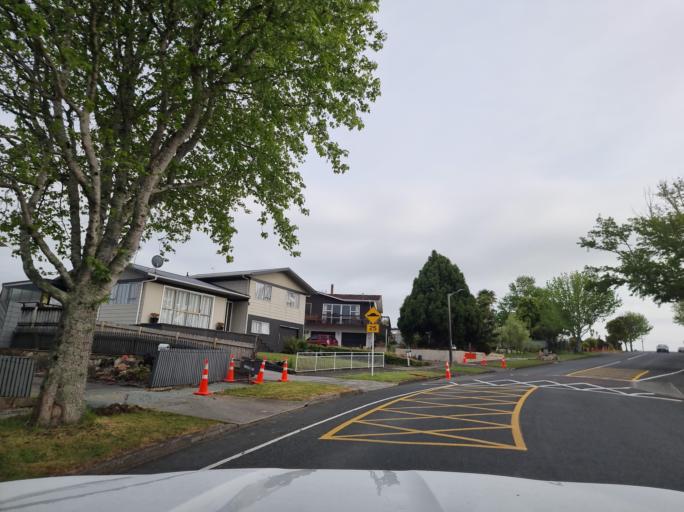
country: NZ
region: Northland
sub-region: Whangarei
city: Whangarei
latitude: -35.7510
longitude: 174.3610
